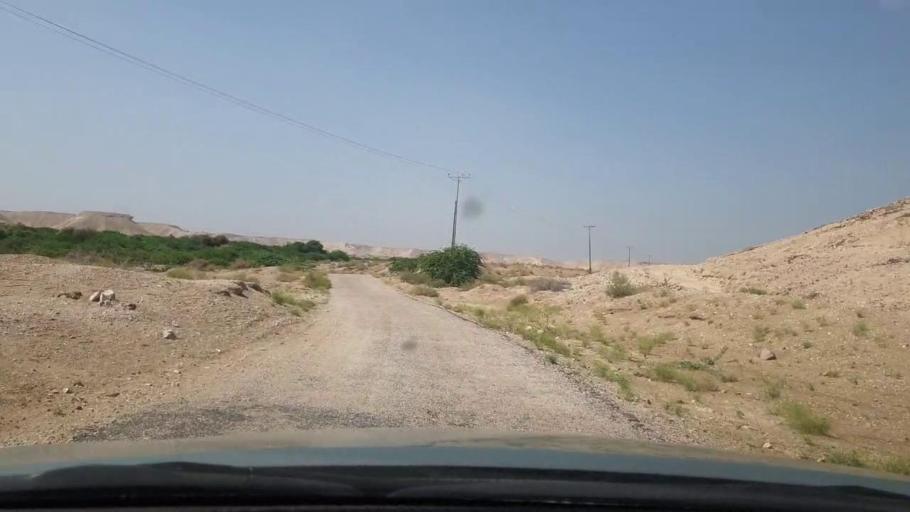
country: PK
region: Sindh
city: Kot Diji
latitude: 27.3333
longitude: 68.8169
